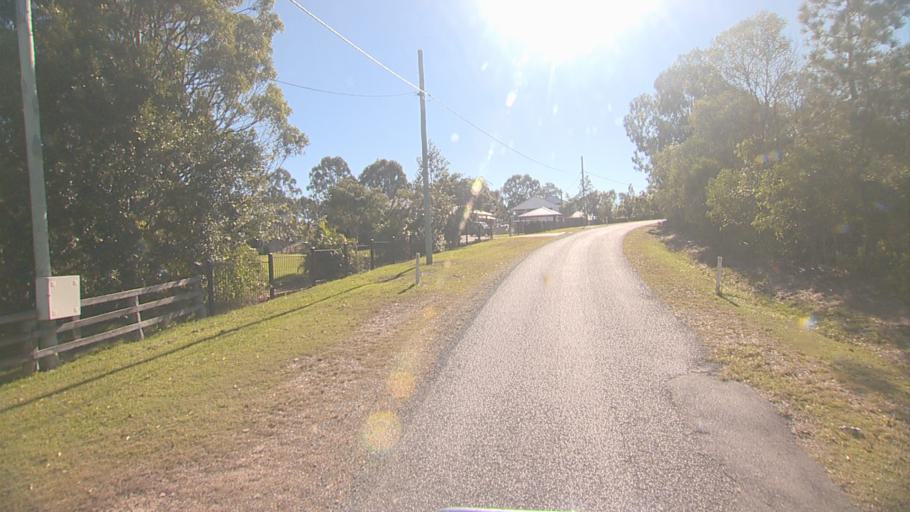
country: AU
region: Queensland
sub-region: Logan
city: Logan Reserve
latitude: -27.7449
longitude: 153.1241
